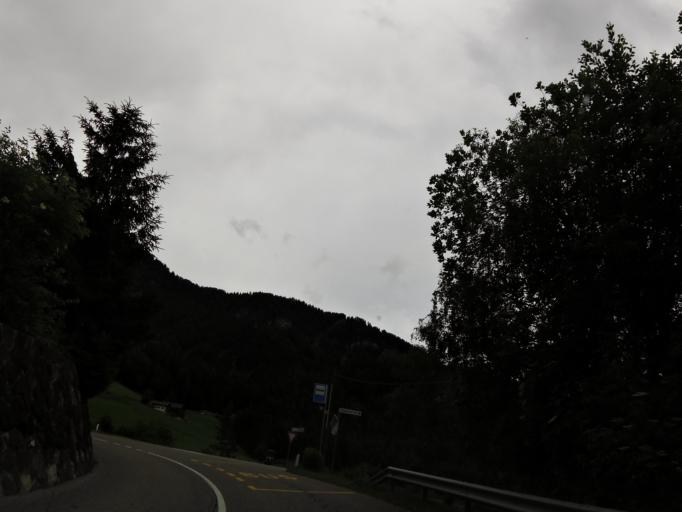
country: IT
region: Trentino-Alto Adige
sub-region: Bolzano
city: Siusi
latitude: 46.5508
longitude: 11.5763
